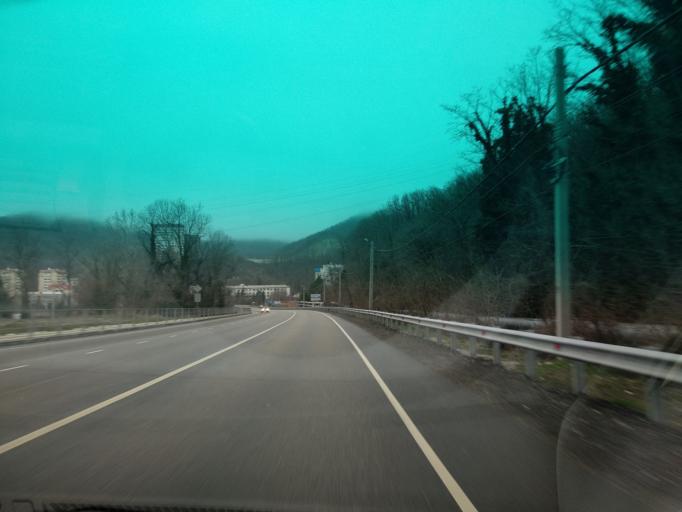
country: RU
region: Krasnodarskiy
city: Tuapse
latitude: 44.1134
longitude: 39.0702
